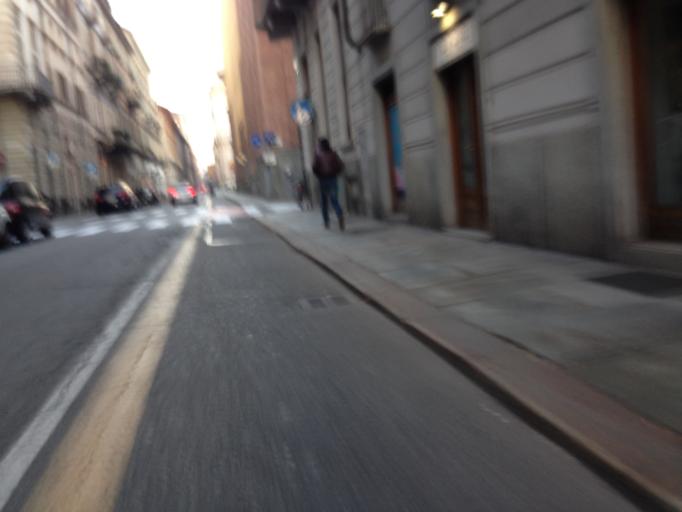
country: IT
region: Piedmont
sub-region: Provincia di Torino
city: Turin
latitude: 45.0678
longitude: 7.6875
